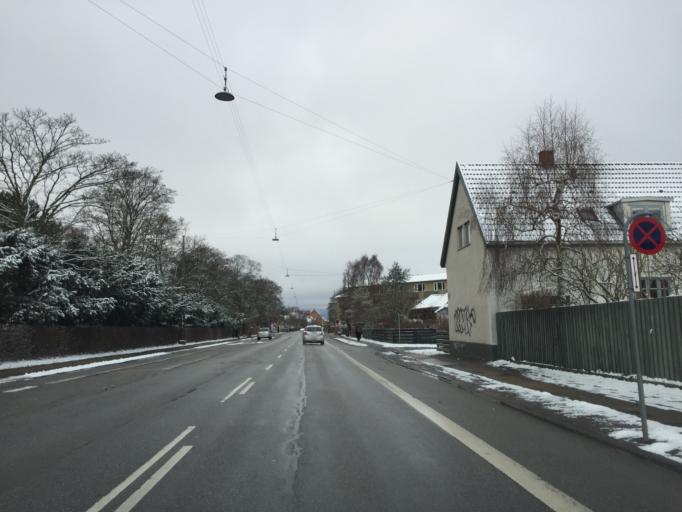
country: DK
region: Capital Region
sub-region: Kobenhavn
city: Christianshavn
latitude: 55.6566
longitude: 12.6214
